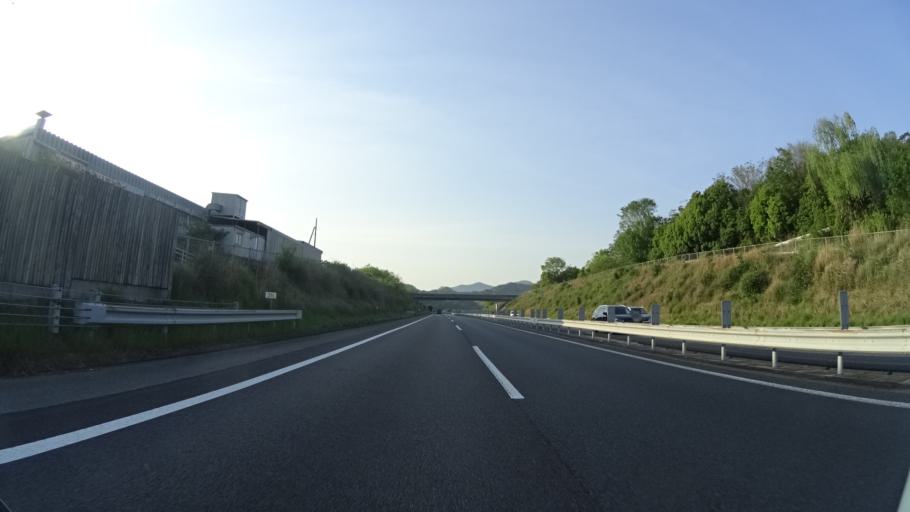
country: JP
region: Kagawa
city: Tadotsu
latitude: 34.1866
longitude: 133.7336
